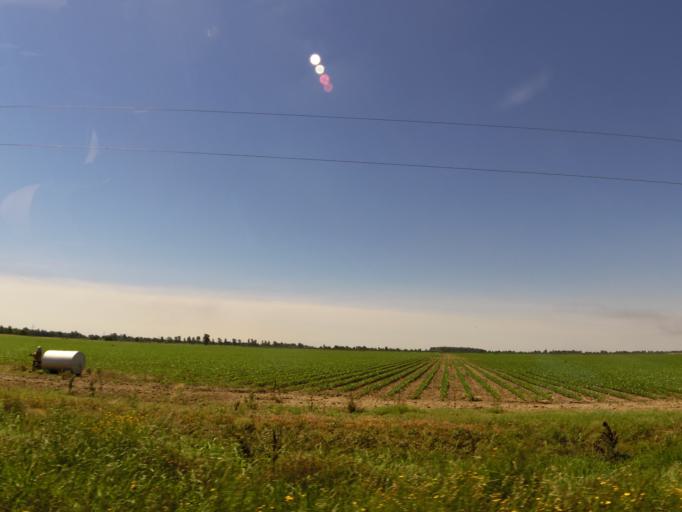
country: US
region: Missouri
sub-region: New Madrid County
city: Lilbourn
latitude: 36.5538
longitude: -89.6893
